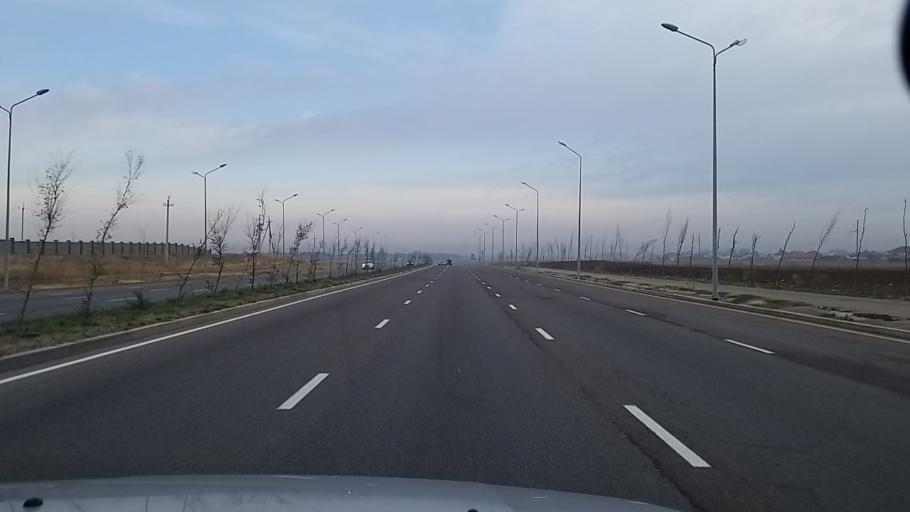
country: KZ
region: Almaty Oblysy
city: Burunday
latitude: 43.3396
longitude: 76.8337
